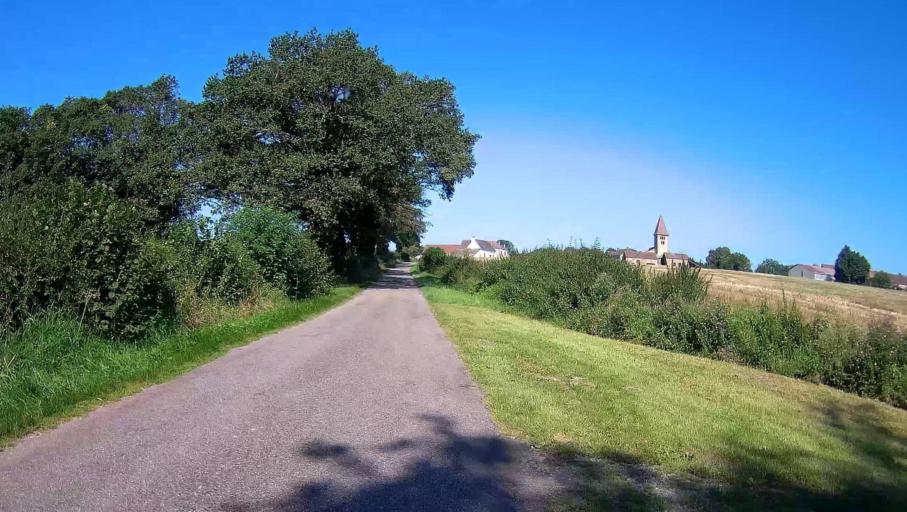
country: FR
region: Bourgogne
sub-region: Departement de Saone-et-Loire
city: Couches
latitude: 46.8344
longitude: 4.5904
